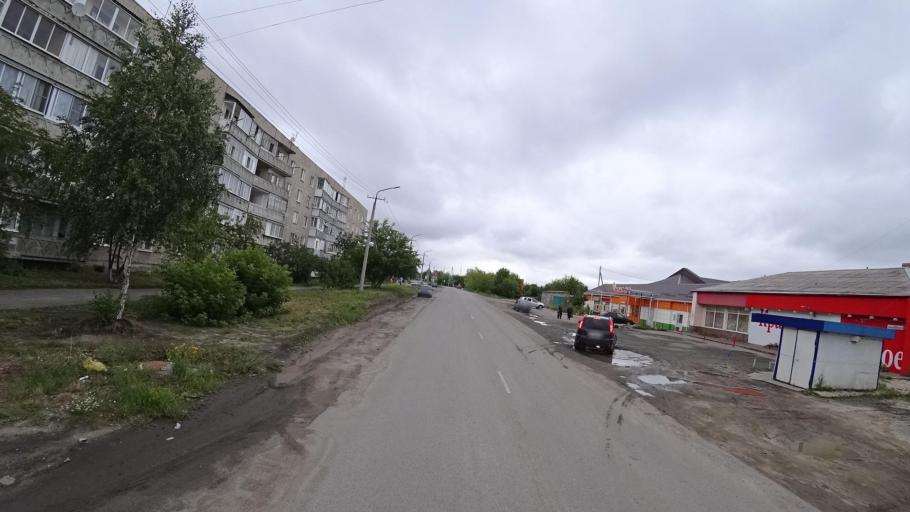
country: RU
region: Sverdlovsk
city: Kamyshlov
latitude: 56.8373
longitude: 62.7303
